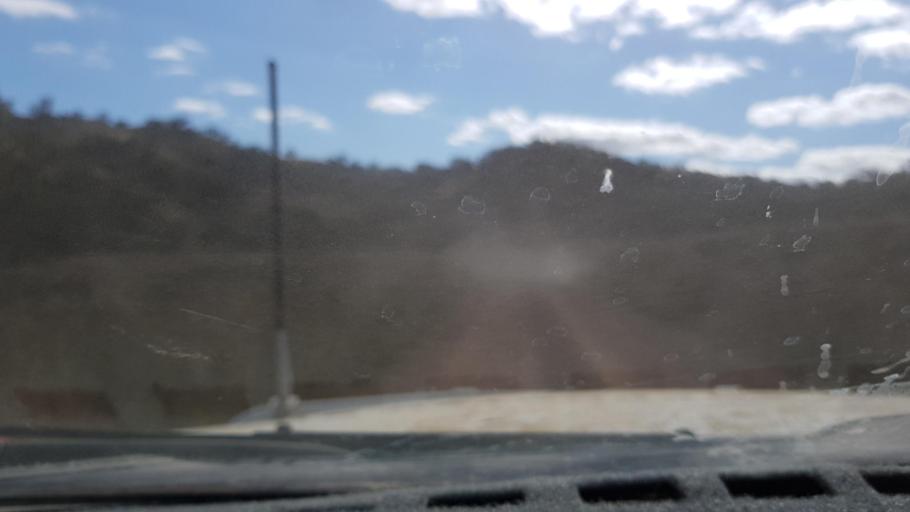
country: AU
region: New South Wales
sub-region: Tamworth Municipality
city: Manilla
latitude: -30.4356
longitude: 150.7899
